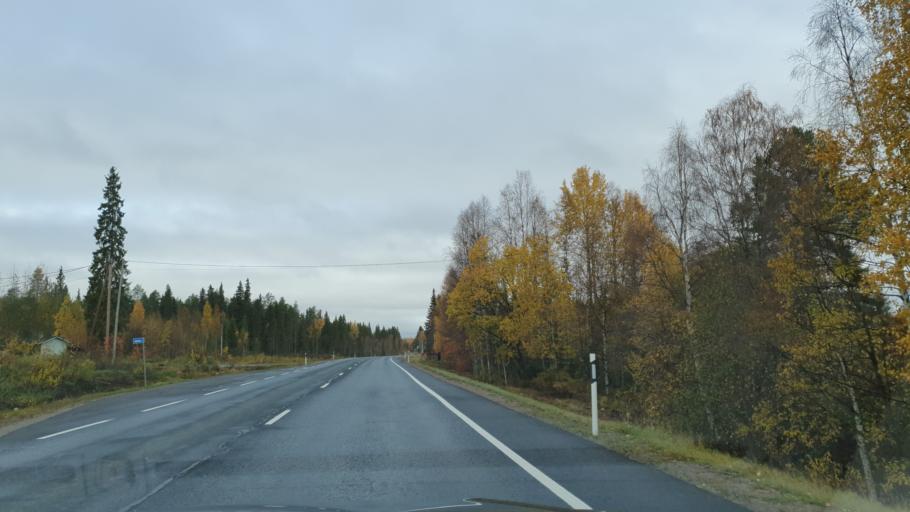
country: FI
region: Lapland
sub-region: Rovaniemi
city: Rovaniemi
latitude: 66.6218
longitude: 25.5377
